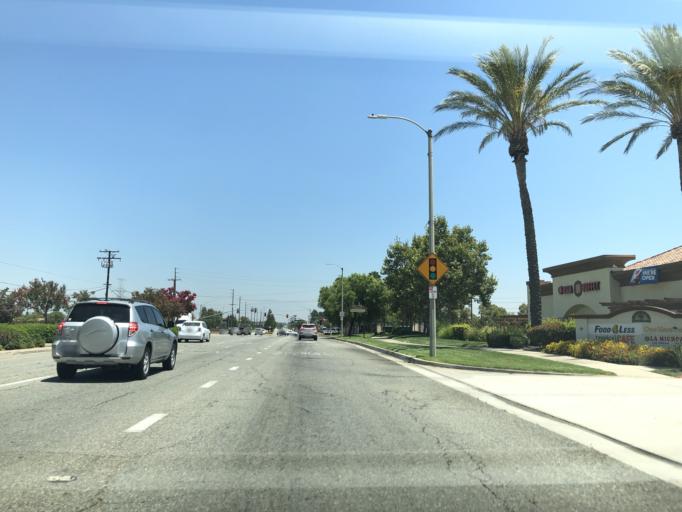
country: US
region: California
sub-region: San Bernardino County
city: Rancho Cucamonga
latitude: 34.1062
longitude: -117.5259
